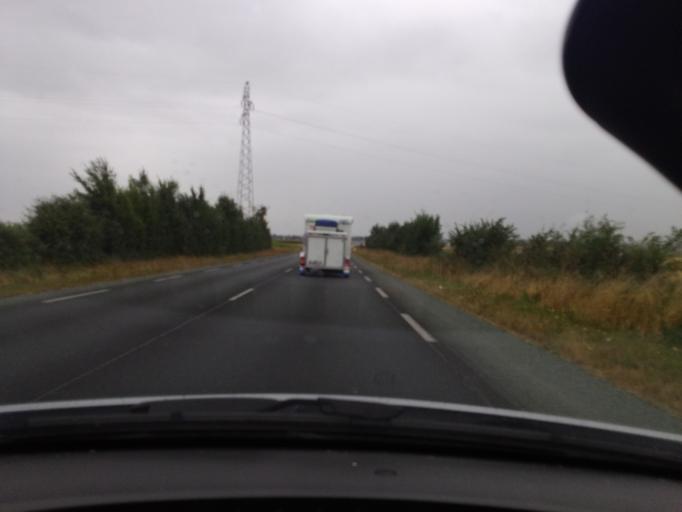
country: FR
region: Pays de la Loire
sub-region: Departement de la Vendee
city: Sainte-Gemme-la-Plaine
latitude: 46.4999
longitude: -1.1015
